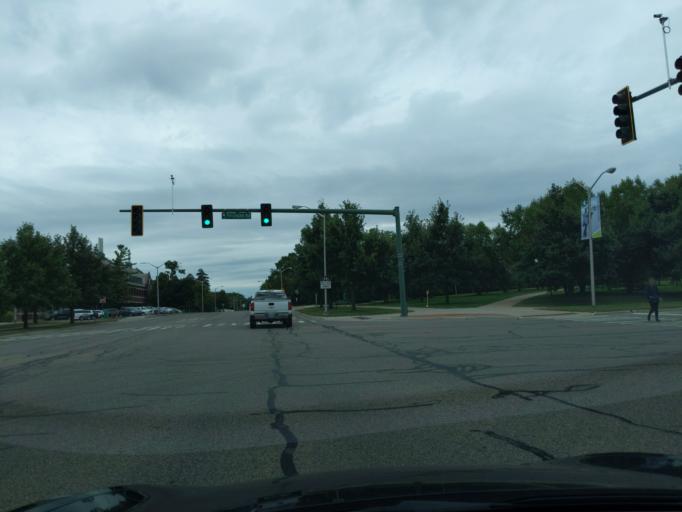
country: US
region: Michigan
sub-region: Ingham County
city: East Lansing
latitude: 42.7231
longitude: -84.4779
